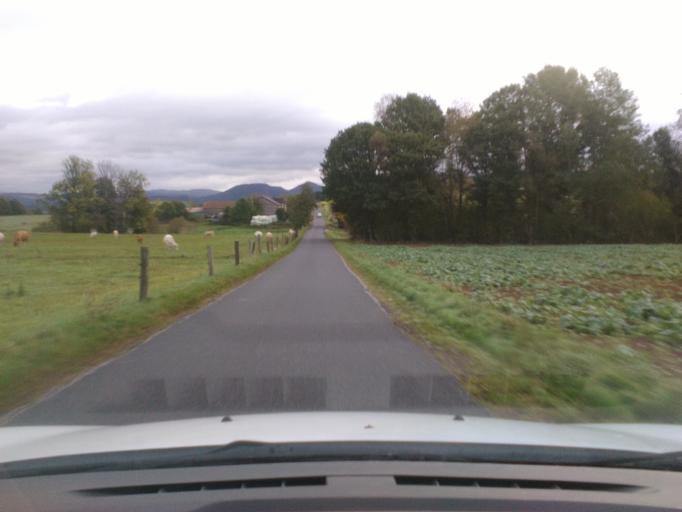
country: FR
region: Lorraine
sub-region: Departement des Vosges
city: Saint-Michel-sur-Meurthe
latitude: 48.3213
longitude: 6.8607
